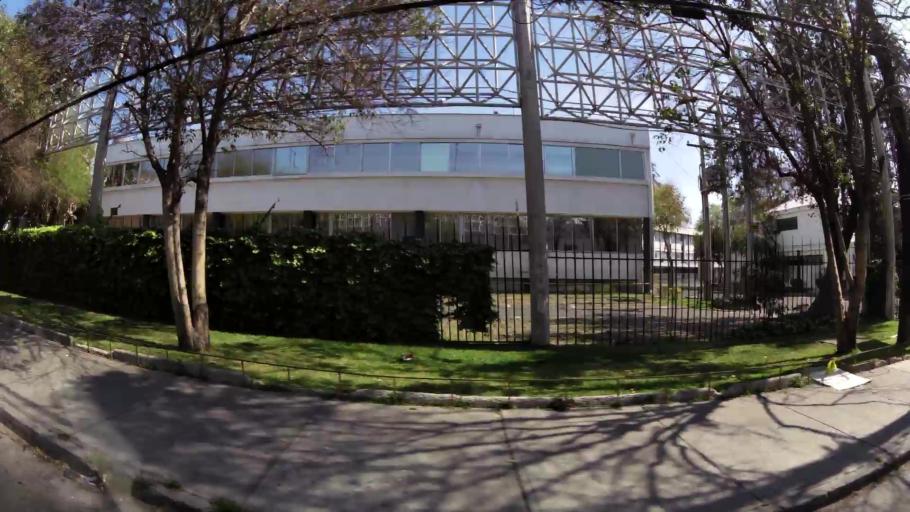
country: CL
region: Santiago Metropolitan
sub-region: Provincia de Santiago
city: Santiago
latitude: -33.4250
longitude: -70.6724
